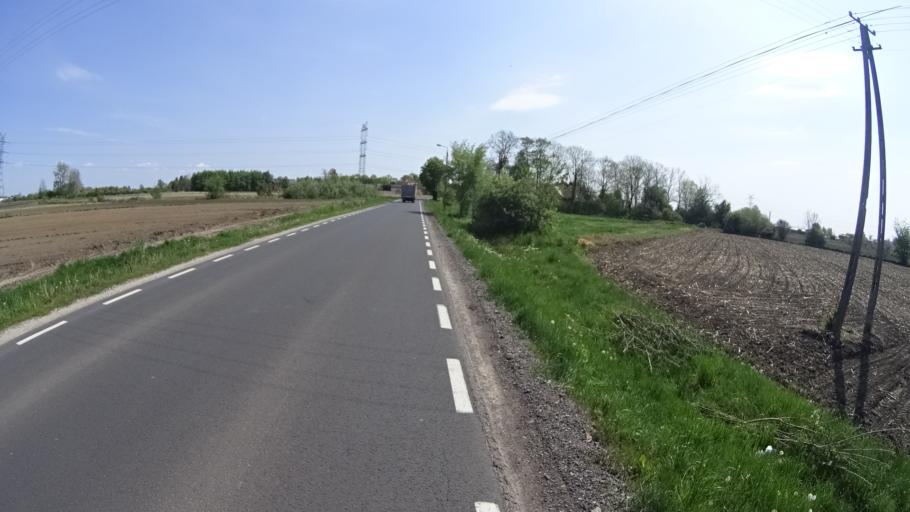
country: PL
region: Masovian Voivodeship
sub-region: Powiat warszawski zachodni
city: Ozarow Mazowiecki
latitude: 52.2347
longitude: 20.7586
